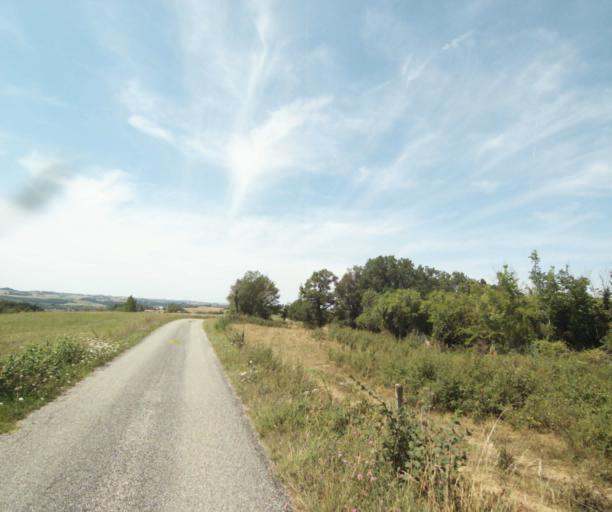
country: FR
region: Midi-Pyrenees
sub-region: Departement de la Haute-Garonne
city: Gaillac-Toulza
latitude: 43.2243
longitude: 1.4131
